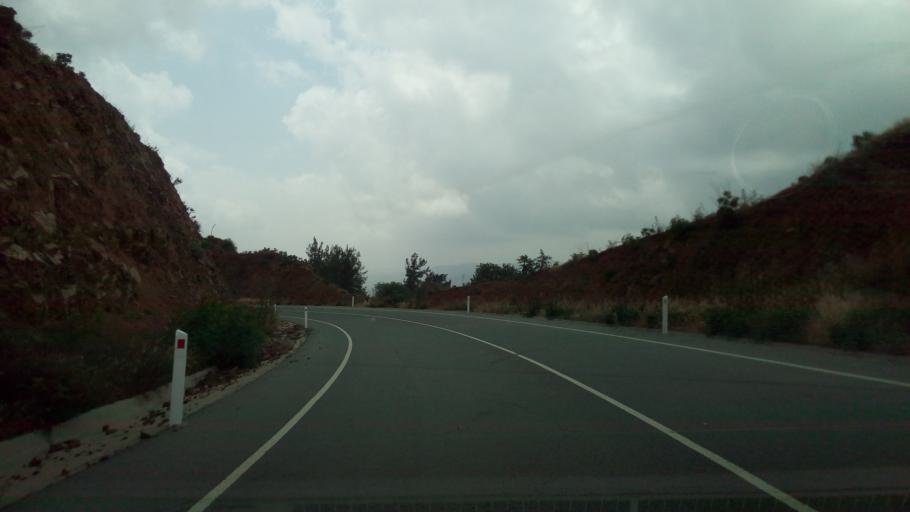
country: CY
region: Limassol
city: Pelendri
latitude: 34.8713
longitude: 32.9982
